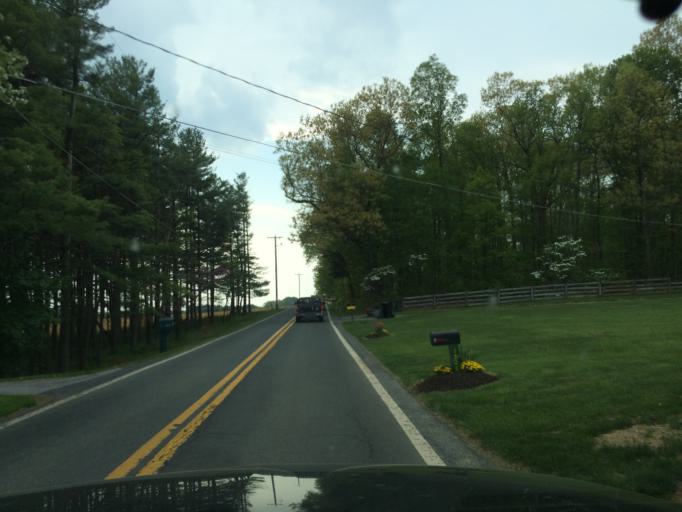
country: US
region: Maryland
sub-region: Carroll County
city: Sykesville
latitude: 39.4026
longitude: -77.0412
